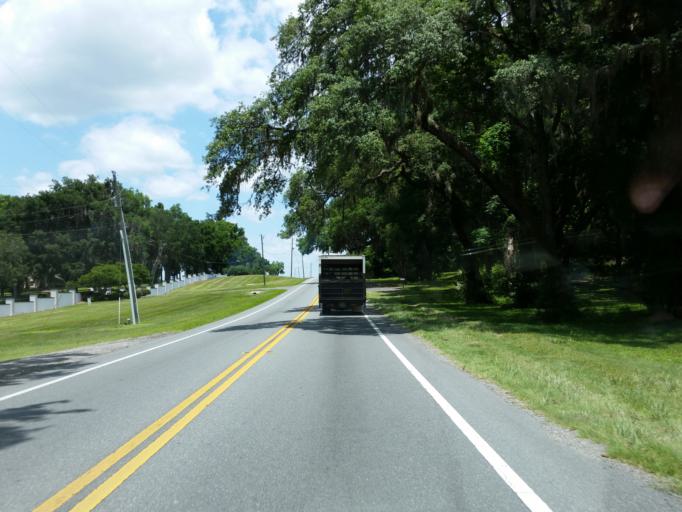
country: US
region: Florida
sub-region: Marion County
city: Belleview
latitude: 28.9892
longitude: -82.0413
